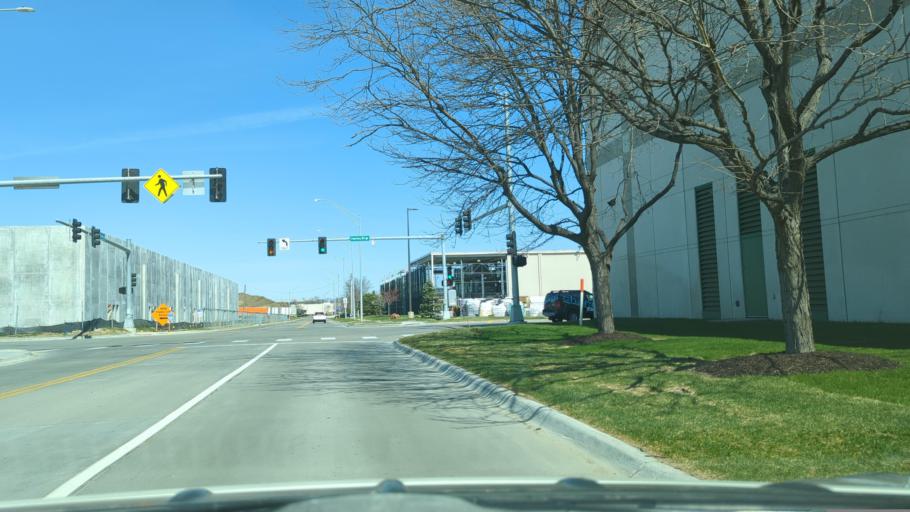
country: US
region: Nebraska
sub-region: Douglas County
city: Ralston
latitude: 41.2561
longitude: -96.0296
